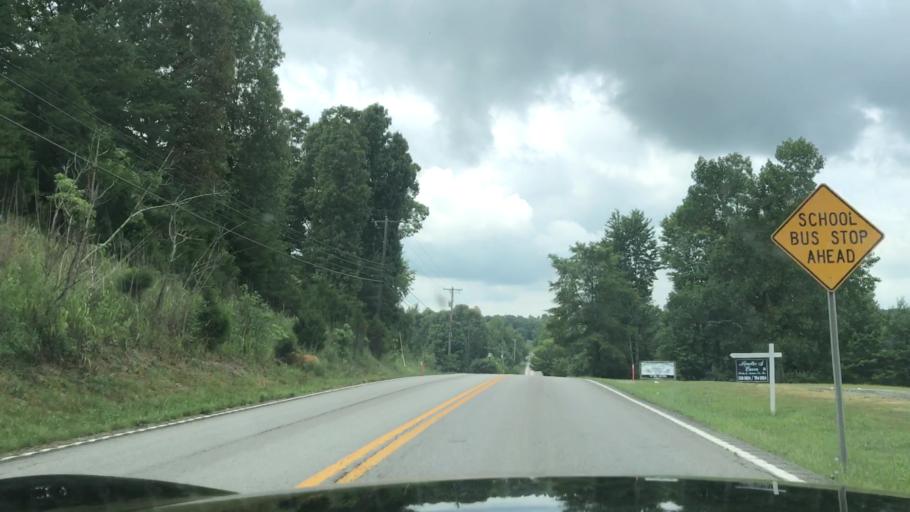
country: US
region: Kentucky
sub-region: Muhlenberg County
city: Central City
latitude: 37.2120
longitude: -87.0652
